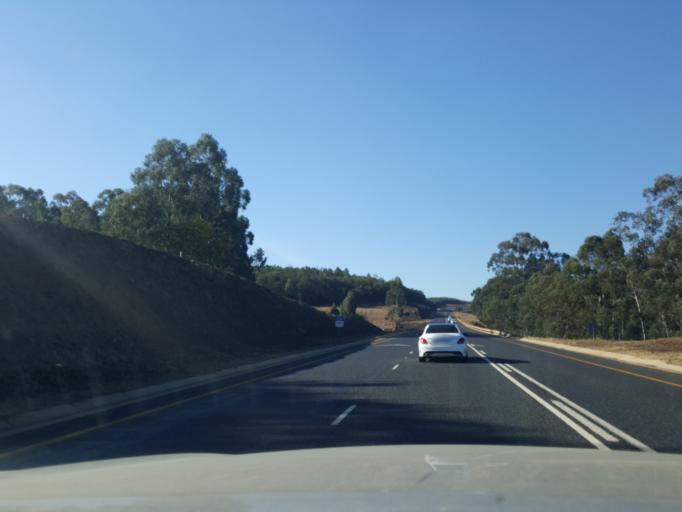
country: ZA
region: Mpumalanga
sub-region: Nkangala District Municipality
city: Belfast
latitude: -25.5442
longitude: 30.3255
